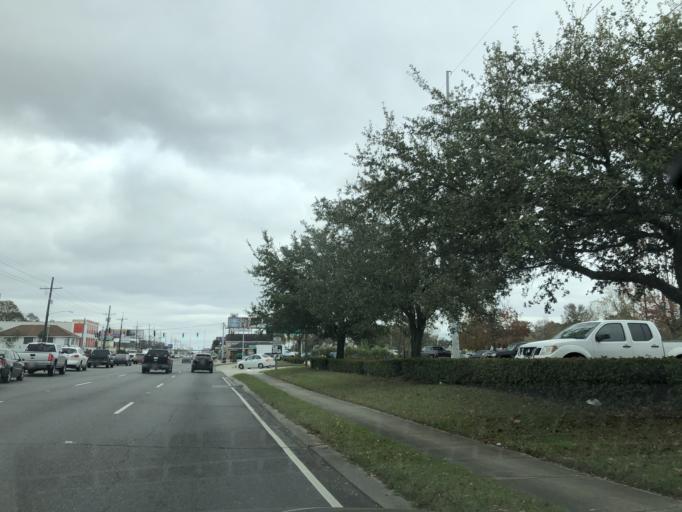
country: US
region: Louisiana
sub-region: Jefferson Parish
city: Metairie Terrace
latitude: 29.9751
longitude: -90.1709
